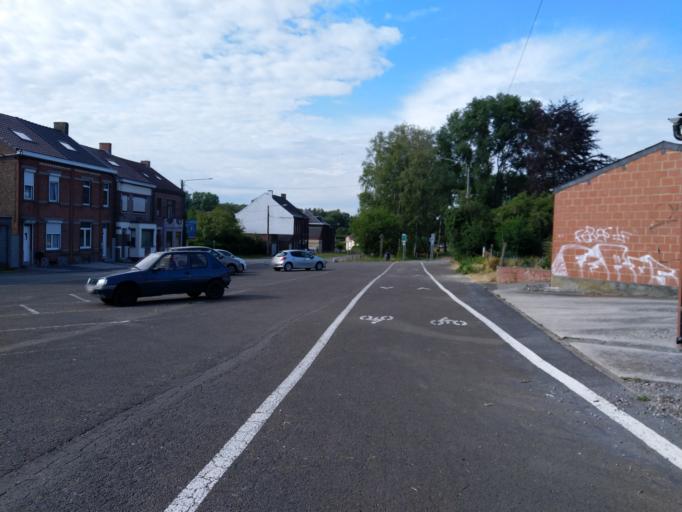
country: BE
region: Wallonia
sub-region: Province du Hainaut
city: Erquelinnes
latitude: 50.3090
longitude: 4.1200
